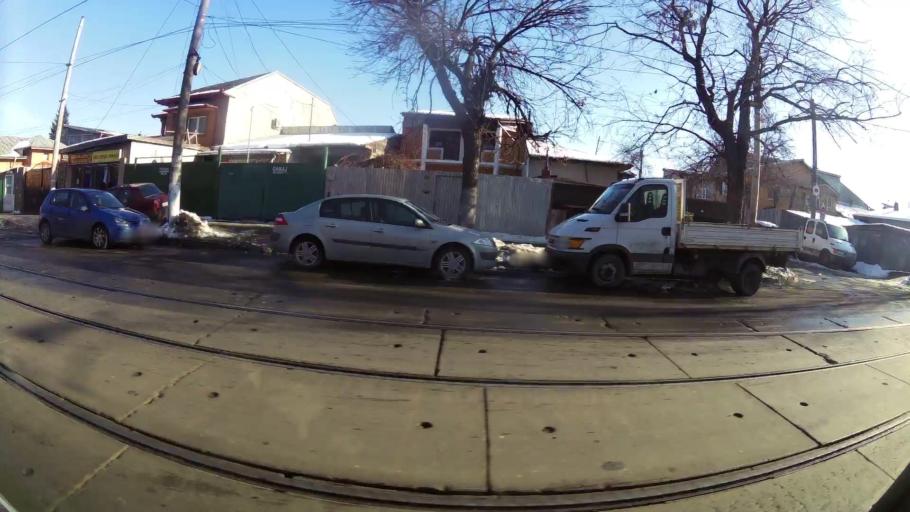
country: RO
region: Bucuresti
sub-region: Municipiul Bucuresti
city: Bucuresti
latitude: 44.3892
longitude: 26.0800
